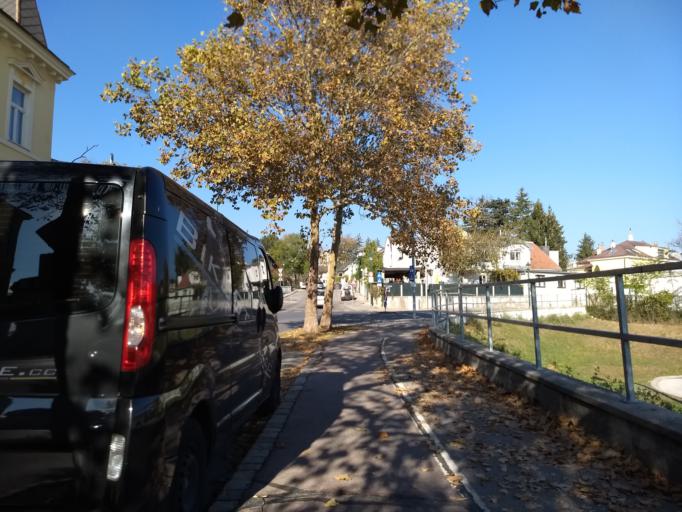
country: AT
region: Lower Austria
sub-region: Politischer Bezirk Modling
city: Maria Enzersdorf
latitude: 48.0941
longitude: 16.2819
